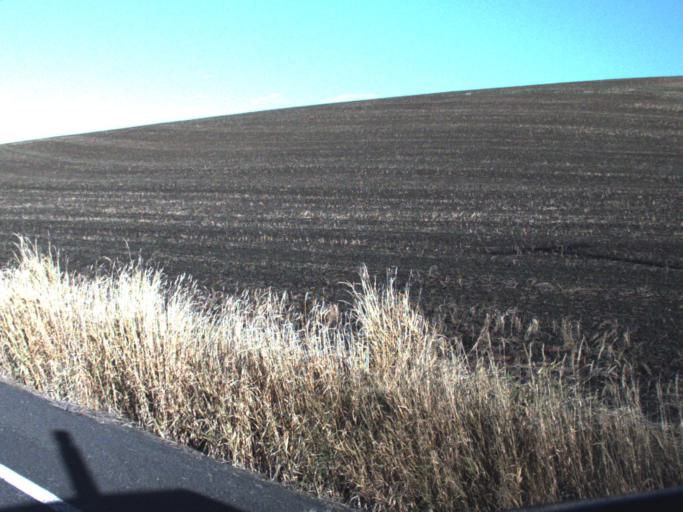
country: US
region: Washington
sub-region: Whitman County
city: Pullman
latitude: 46.7096
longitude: -117.2719
